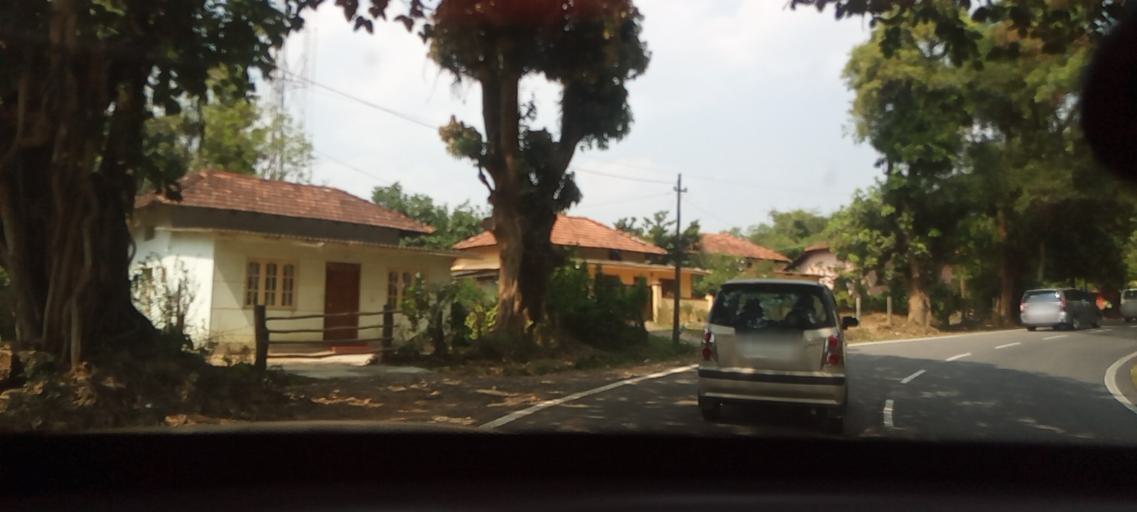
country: IN
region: Karnataka
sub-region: Chikmagalur
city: Chikmagalur
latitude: 13.2651
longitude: 75.6870
